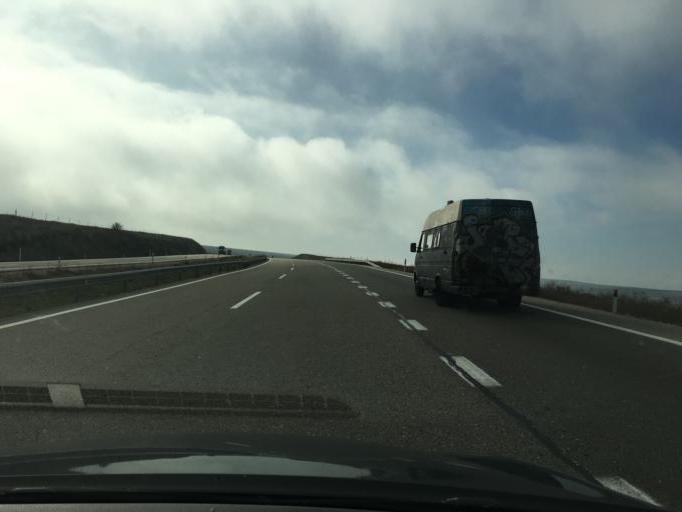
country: ES
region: Castille and Leon
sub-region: Provincia de Burgos
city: Vallarta de Bureba
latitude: 42.6135
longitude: -3.2011
